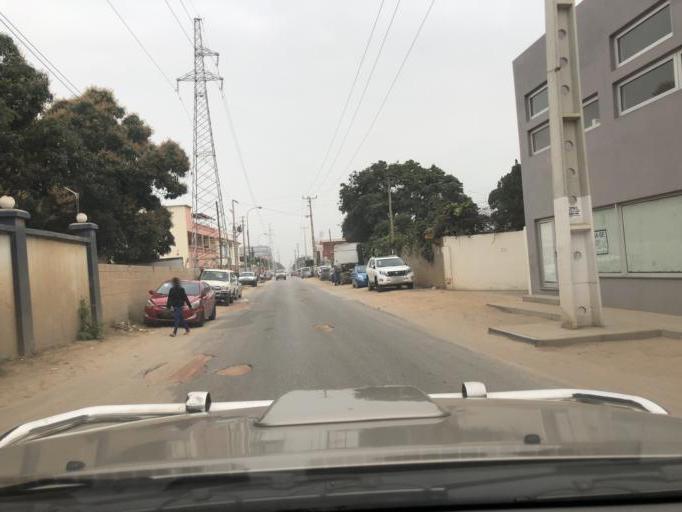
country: AO
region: Luanda
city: Luanda
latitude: -8.8874
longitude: 13.1891
